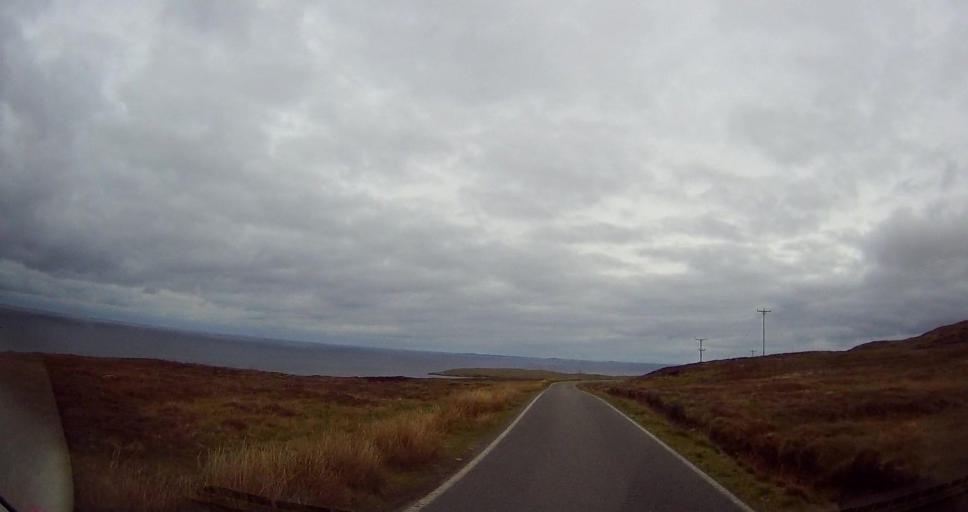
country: GB
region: Scotland
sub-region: Shetland Islands
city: Shetland
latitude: 60.5440
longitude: -1.0547
